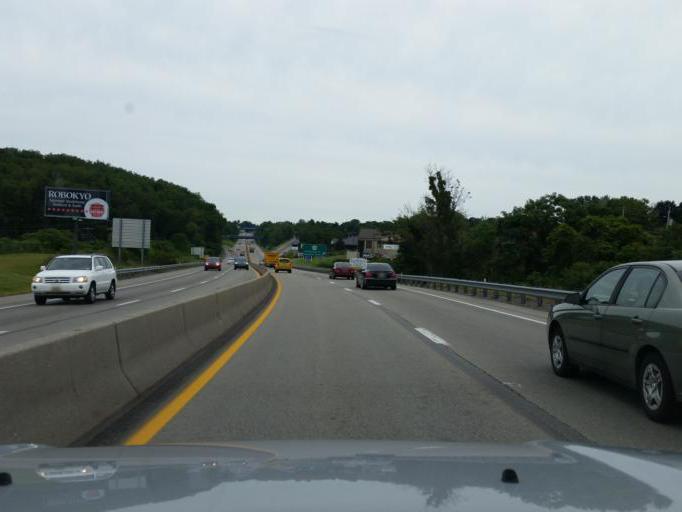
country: US
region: Pennsylvania
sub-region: Westmoreland County
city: Greensburg
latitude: 40.2910
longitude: -79.5257
